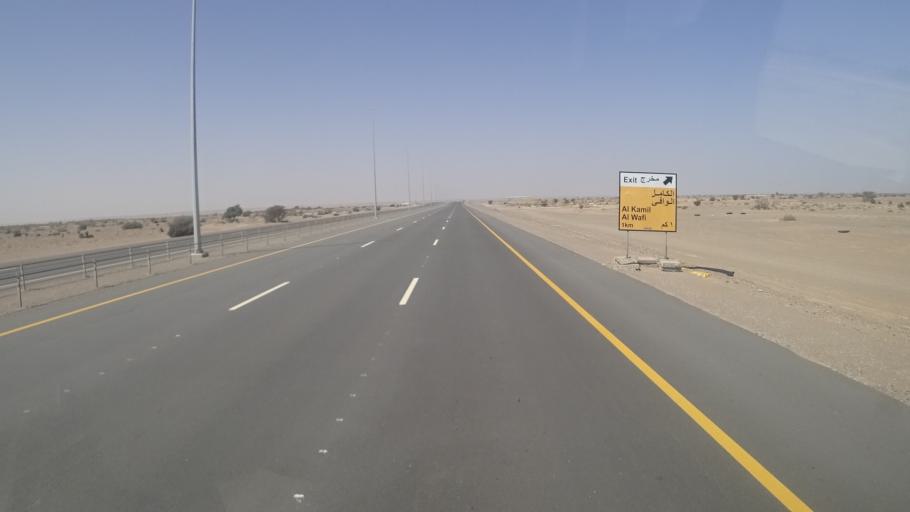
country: OM
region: Ash Sharqiyah
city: Badiyah
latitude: 22.2770
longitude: 59.1853
